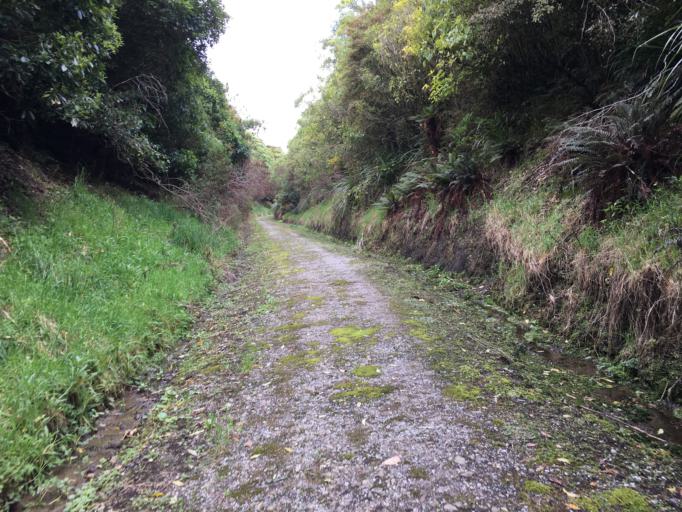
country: NZ
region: Otago
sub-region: Clutha District
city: Papatowai
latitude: -46.5030
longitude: 169.4836
